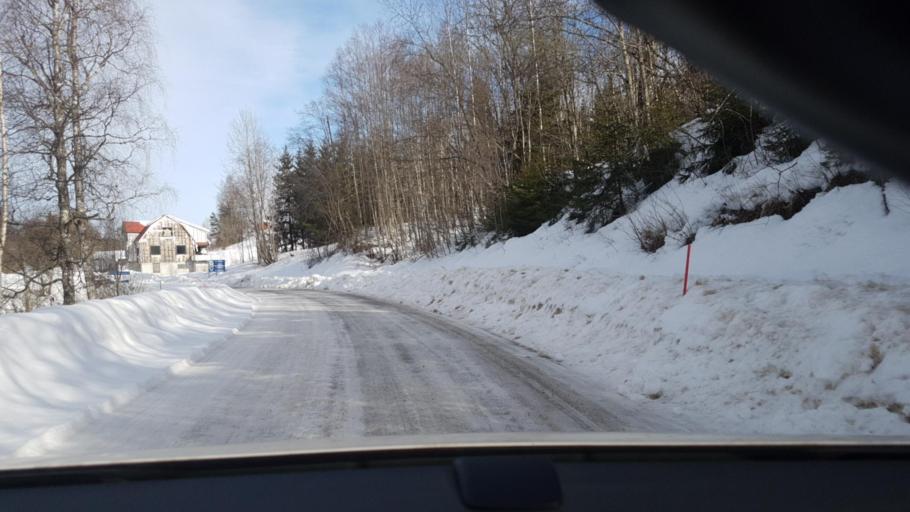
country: NO
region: Hedmark
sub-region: Eidskog
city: Skotterud
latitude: 59.8982
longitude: 11.9872
